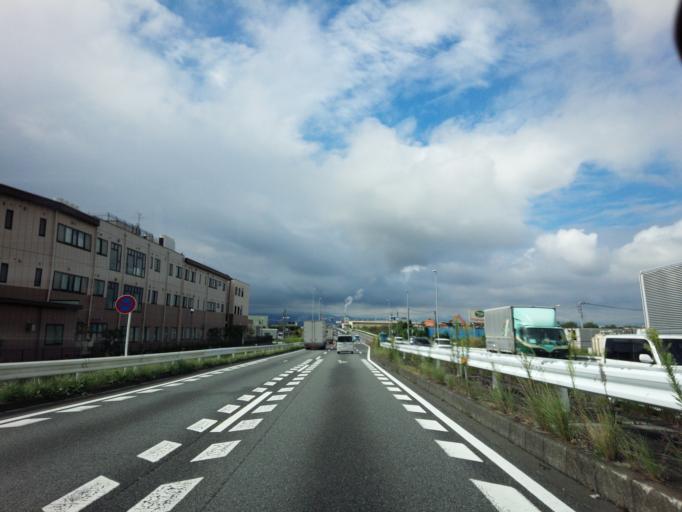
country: JP
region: Shizuoka
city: Fuji
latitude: 35.1378
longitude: 138.7495
